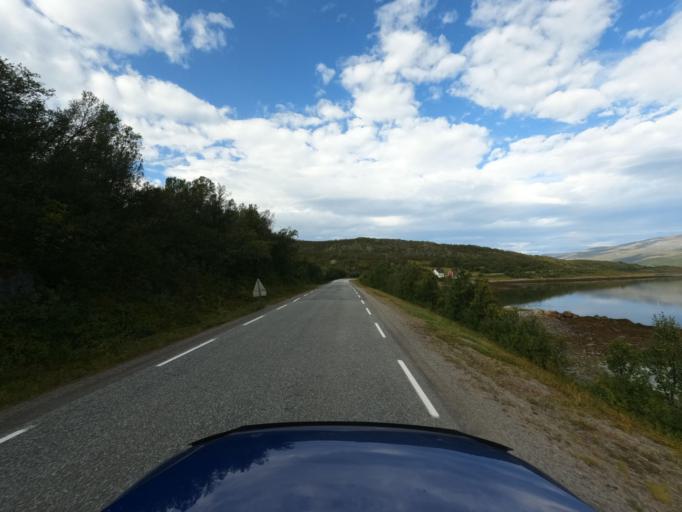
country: NO
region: Finnmark Fylke
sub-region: Kvalsund
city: Kvalsund
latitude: 70.4593
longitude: 24.2703
